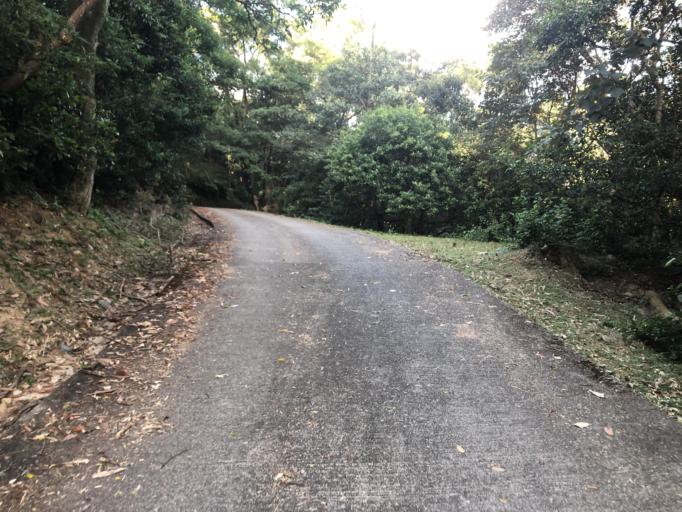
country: HK
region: Tsuen Wan
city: Tsuen Wan
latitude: 22.3918
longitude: 114.0856
